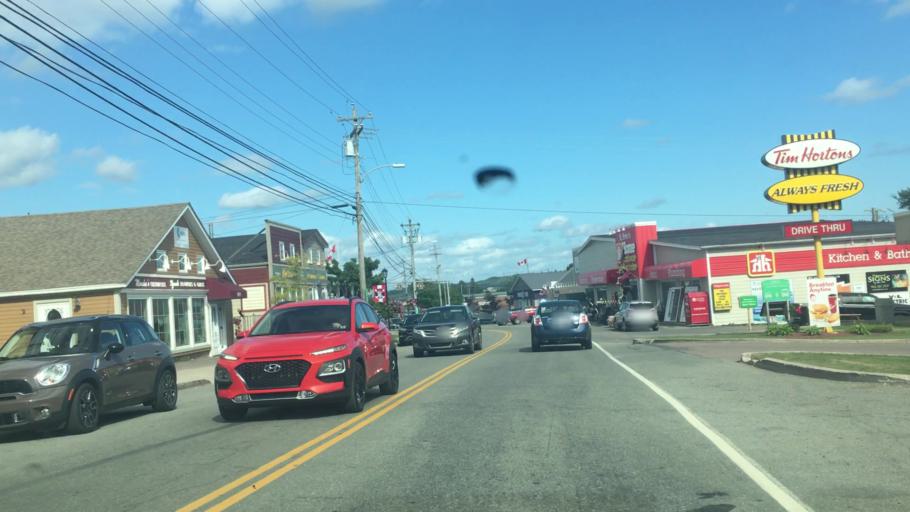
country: CA
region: Nova Scotia
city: Princeville
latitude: 45.6555
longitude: -60.8768
